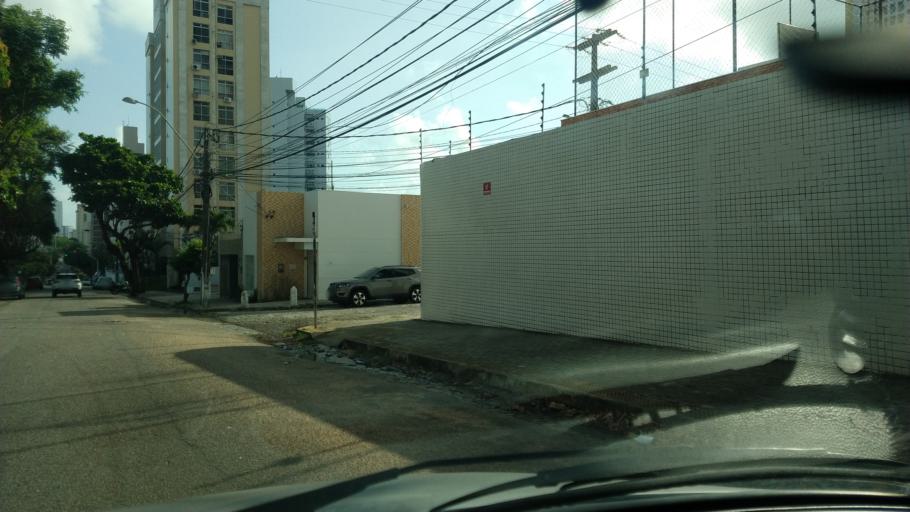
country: BR
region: Rio Grande do Norte
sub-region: Natal
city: Natal
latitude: -5.7996
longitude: -35.2029
